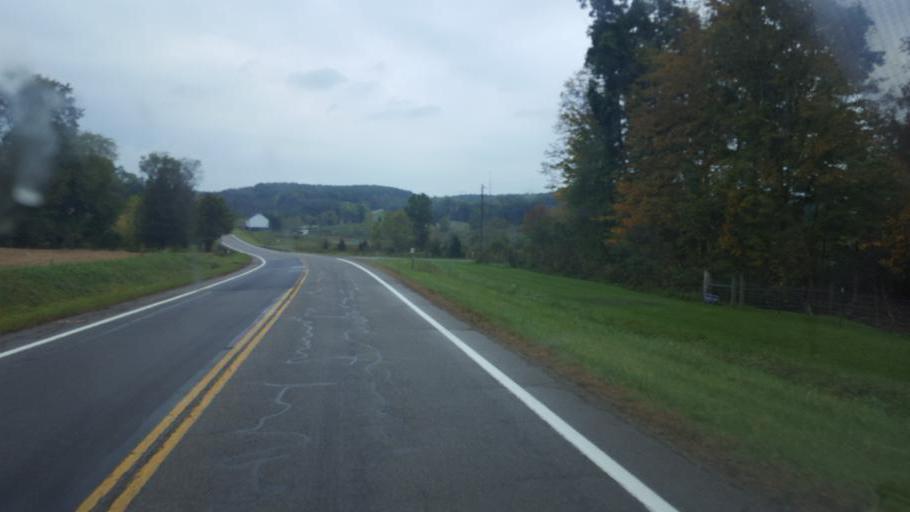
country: US
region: Ohio
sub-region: Knox County
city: Danville
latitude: 40.5116
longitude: -82.3262
